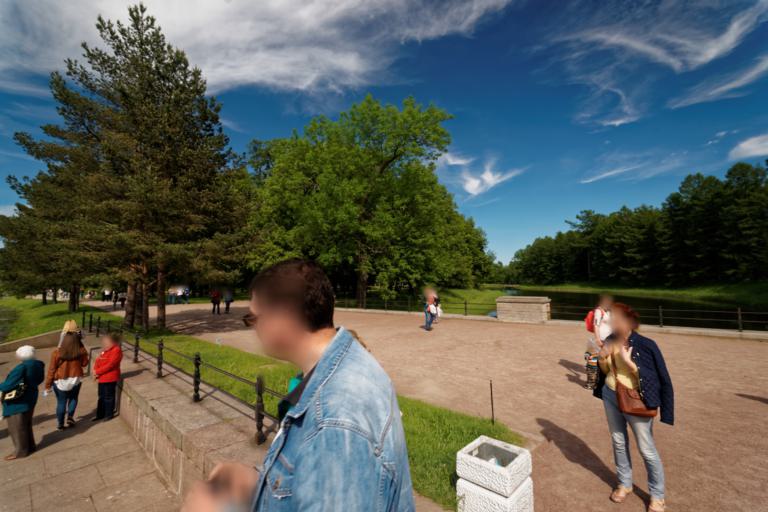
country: RU
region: St.-Petersburg
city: Pushkin
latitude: 59.7112
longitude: 30.3991
